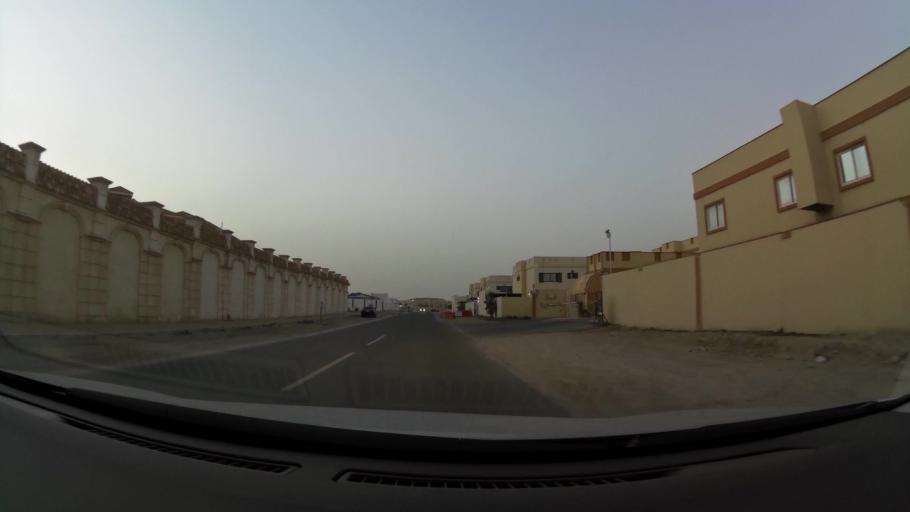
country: QA
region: Baladiyat ar Rayyan
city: Ar Rayyan
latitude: 25.2570
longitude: 51.4577
